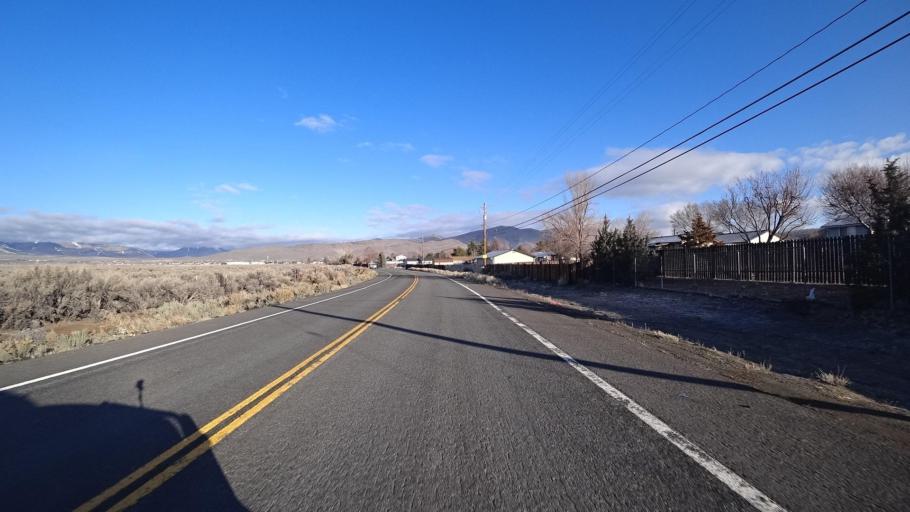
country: US
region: Nevada
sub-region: Washoe County
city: Cold Springs
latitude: 39.6685
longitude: -119.9611
